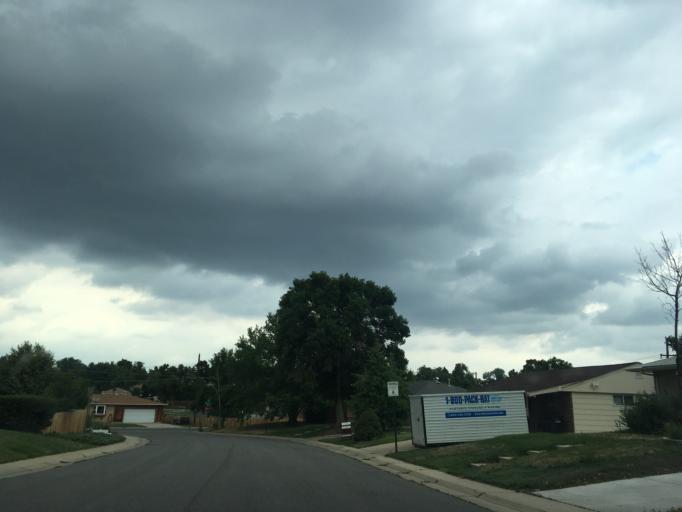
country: US
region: Colorado
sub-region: Arapahoe County
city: Sheridan
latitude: 39.6875
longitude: -105.0168
